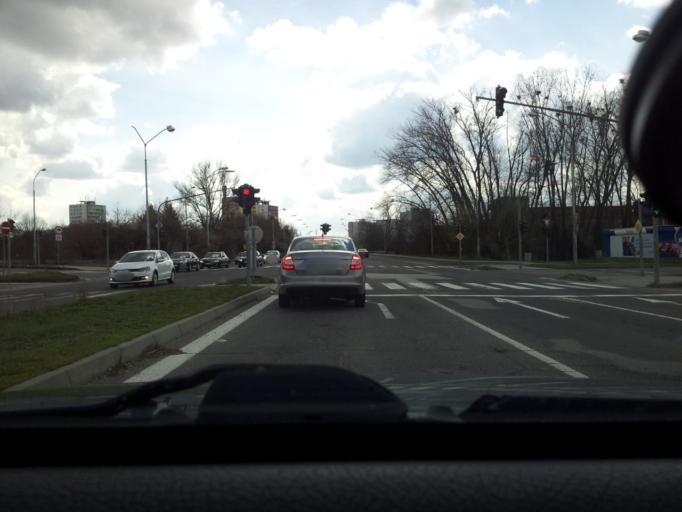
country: SK
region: Nitriansky
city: Levice
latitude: 48.2231
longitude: 18.5991
